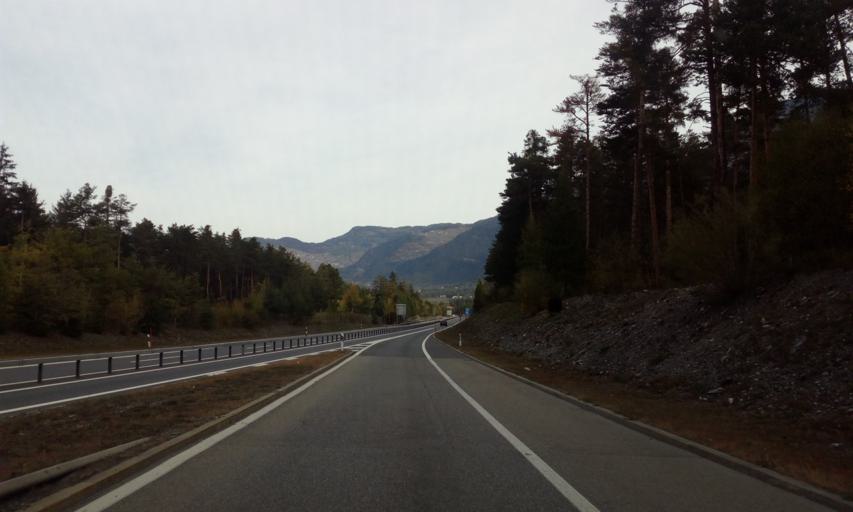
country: CH
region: Grisons
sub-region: Hinterrhein District
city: Thusis
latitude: 46.6993
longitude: 9.4470
